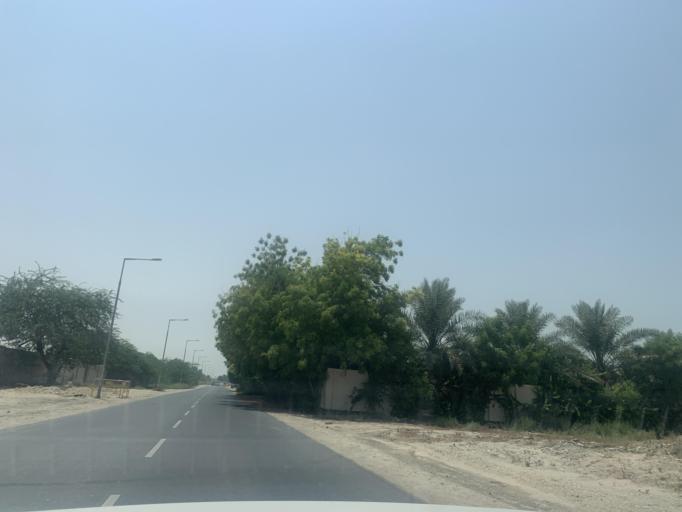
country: BH
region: Central Governorate
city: Madinat Hamad
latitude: 26.1489
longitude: 50.4657
